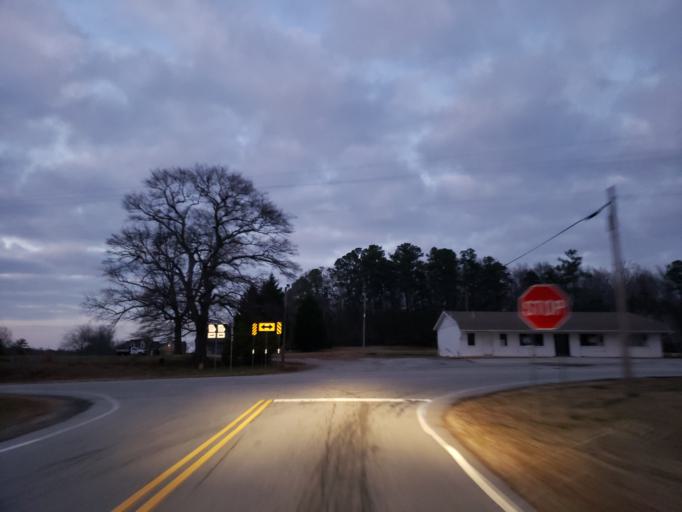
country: US
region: Georgia
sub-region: Carroll County
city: Temple
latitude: 33.8279
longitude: -85.0449
